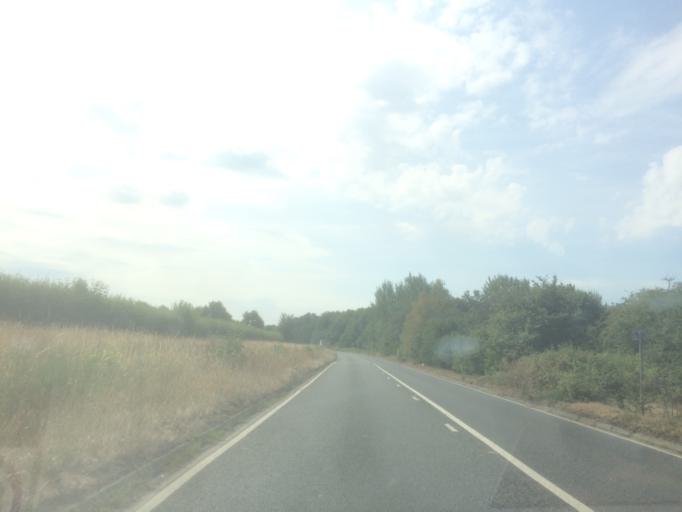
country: GB
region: England
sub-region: Buckinghamshire
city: Farnham Royal
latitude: 51.5763
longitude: -0.6241
